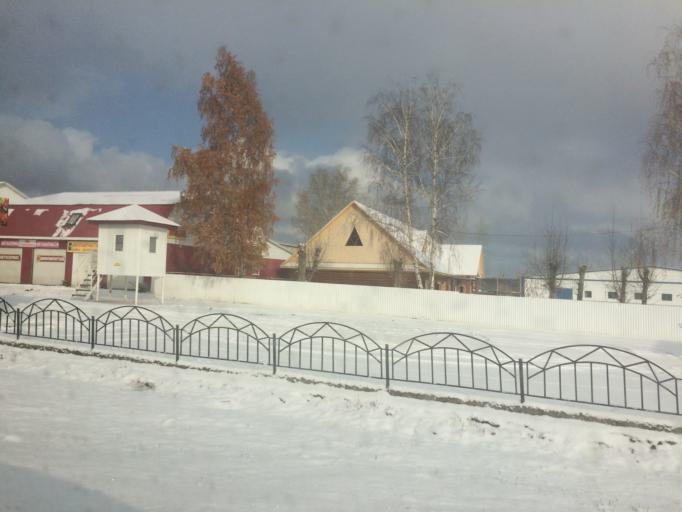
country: RU
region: Bashkortostan
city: Abzakovo
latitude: 53.3345
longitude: 58.5204
